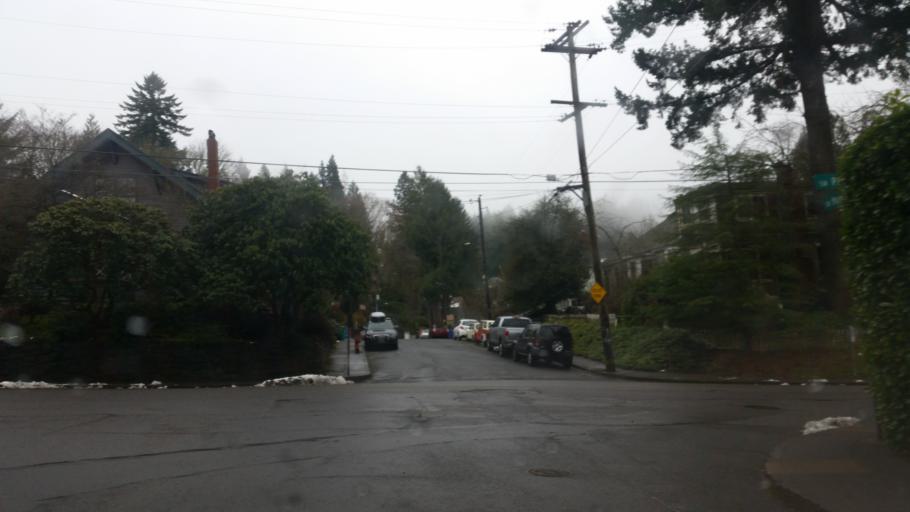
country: US
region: Oregon
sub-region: Multnomah County
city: Portland
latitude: 45.5053
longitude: -122.7052
